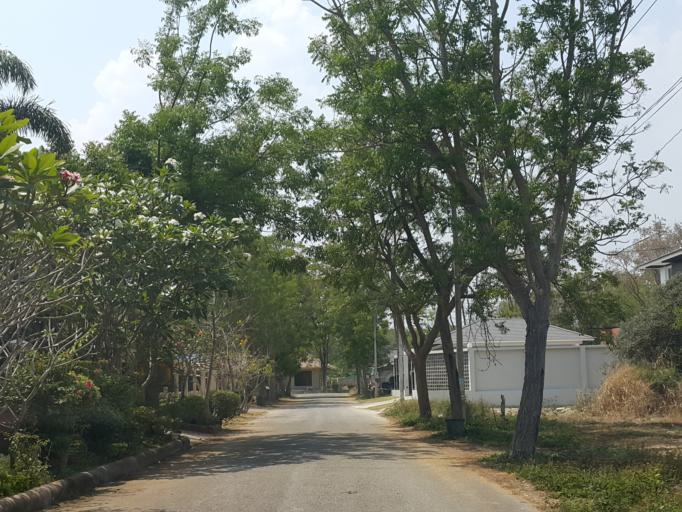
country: TH
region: Chiang Mai
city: Chiang Mai
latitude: 18.7319
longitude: 98.9726
